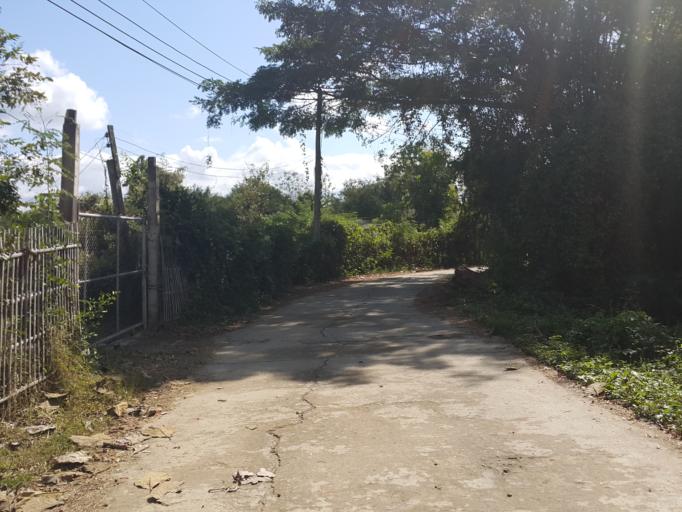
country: TH
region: Chiang Mai
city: San Kamphaeng
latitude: 18.7783
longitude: 99.1137
